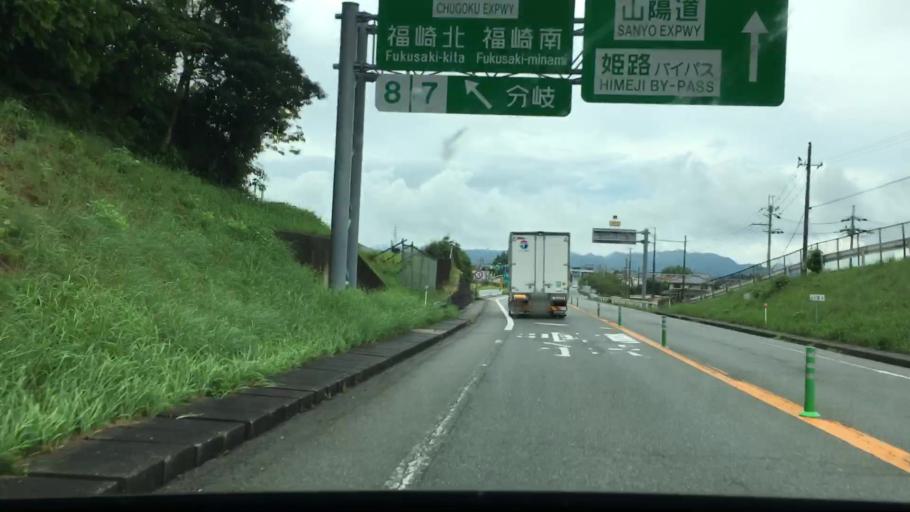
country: JP
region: Hyogo
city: Himeji
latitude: 34.9599
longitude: 134.7699
